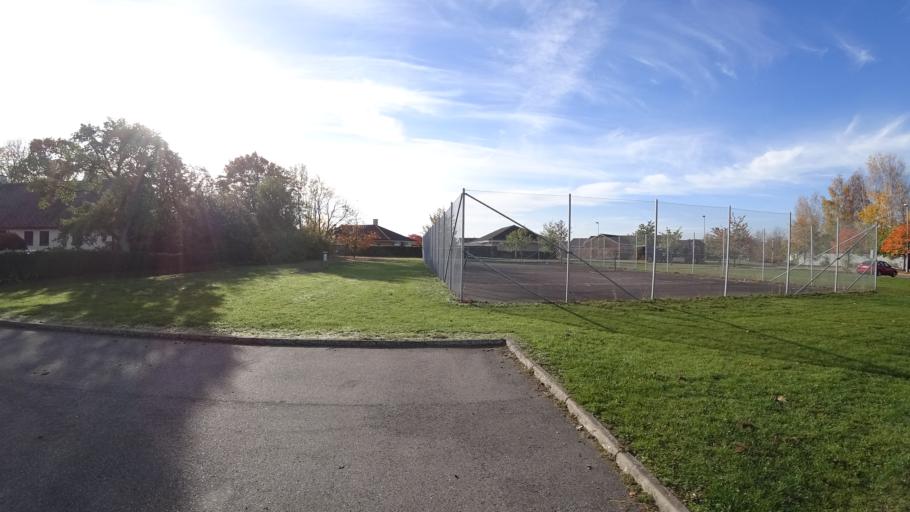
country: SE
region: Skane
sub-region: Staffanstorps Kommun
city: Staffanstorp
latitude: 55.6402
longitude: 13.2268
